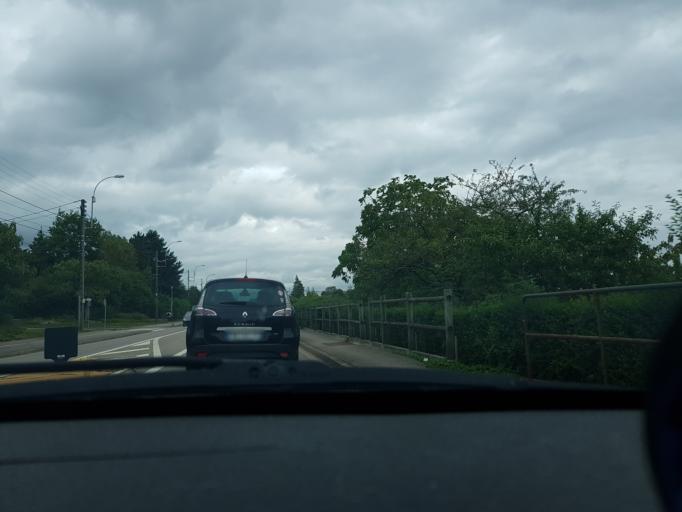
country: FR
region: Lorraine
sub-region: Departement de Meurthe-et-Moselle
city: Seichamps
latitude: 48.7167
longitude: 6.2580
